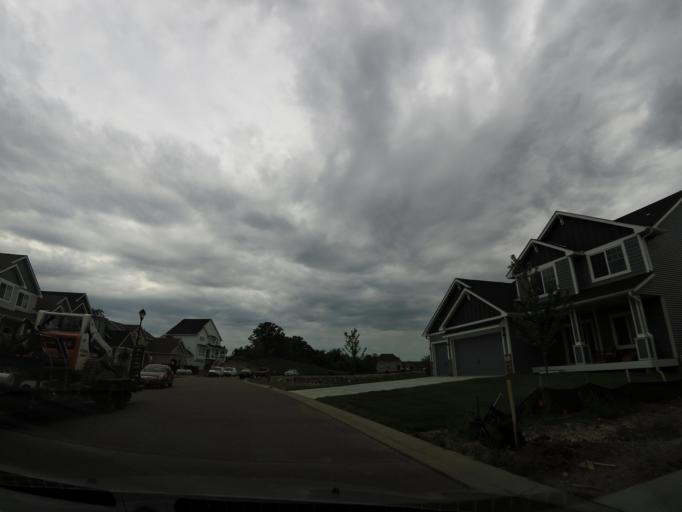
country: US
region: Minnesota
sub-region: Scott County
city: Savage
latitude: 44.7288
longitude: -93.3614
